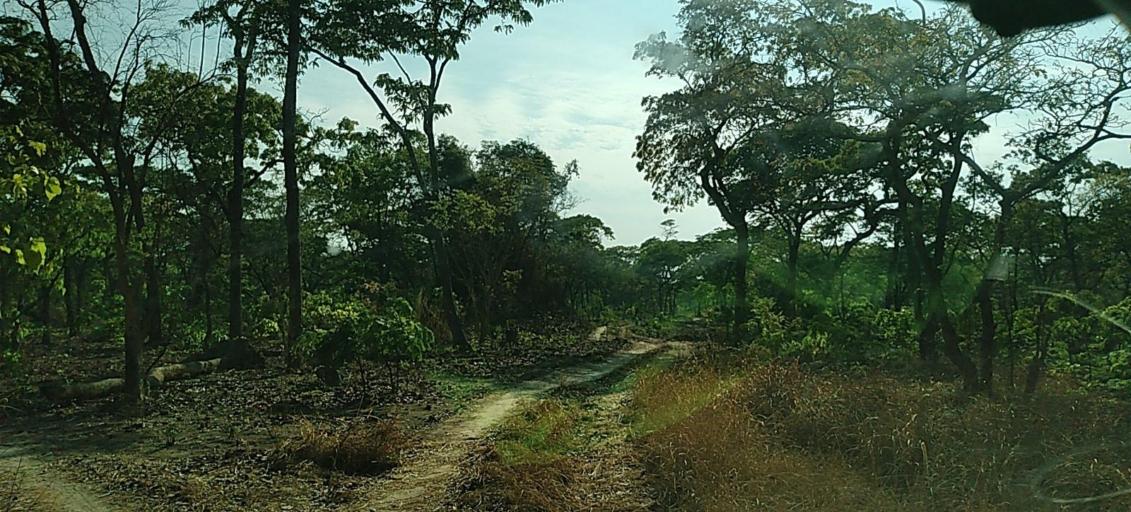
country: ZM
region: North-Western
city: Kalengwa
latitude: -13.2361
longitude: 25.0582
